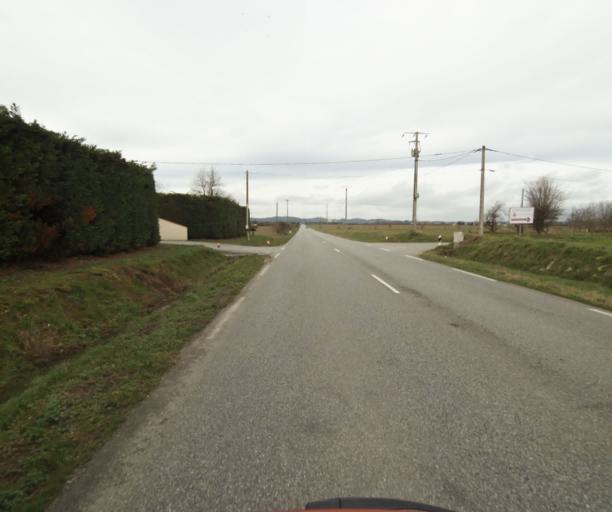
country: FR
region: Midi-Pyrenees
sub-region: Departement de l'Ariege
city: La Tour-du-Crieu
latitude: 43.0938
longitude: 1.6727
